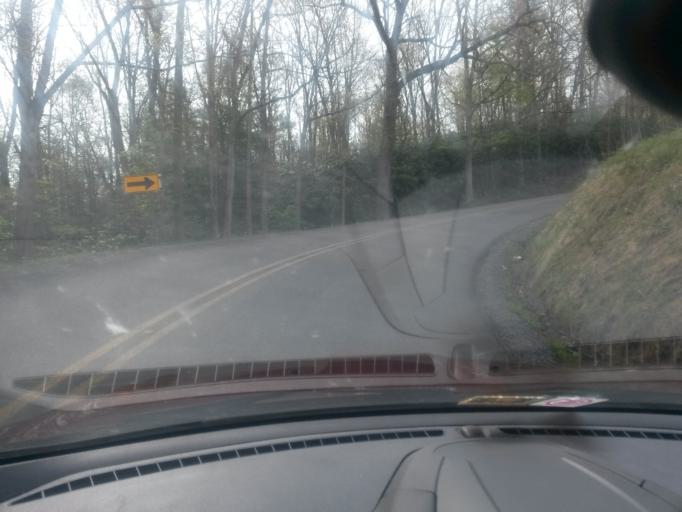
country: US
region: West Virginia
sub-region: Pocahontas County
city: Marlinton
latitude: 38.0958
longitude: -80.2258
